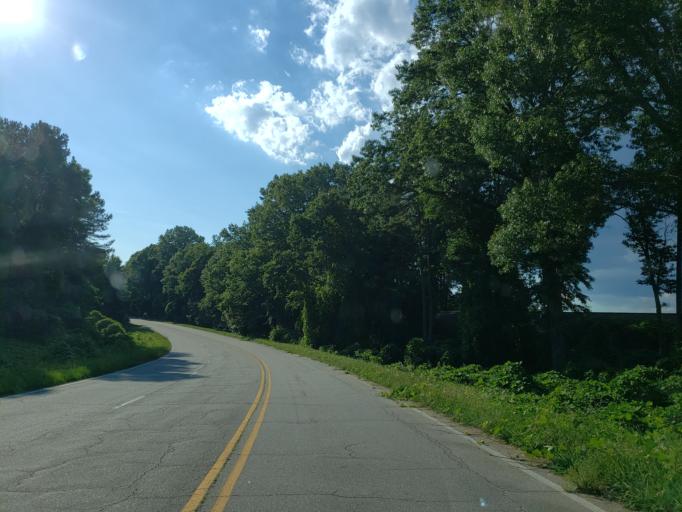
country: US
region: Georgia
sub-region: Haralson County
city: Buchanan
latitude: 33.7856
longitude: -85.1661
